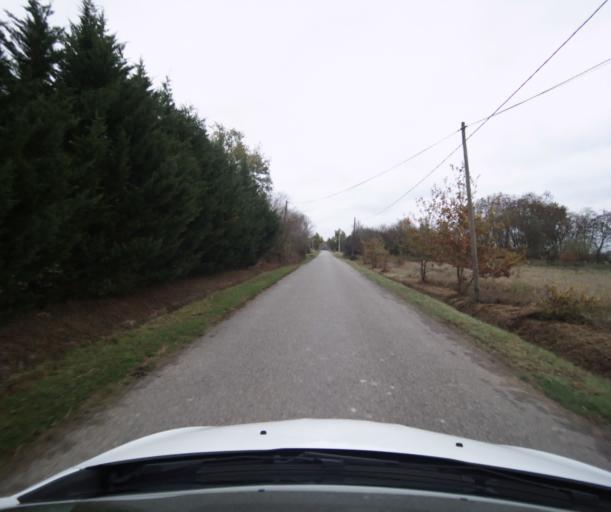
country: FR
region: Midi-Pyrenees
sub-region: Departement du Tarn-et-Garonne
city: Saint-Porquier
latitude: 44.0427
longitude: 1.1725
